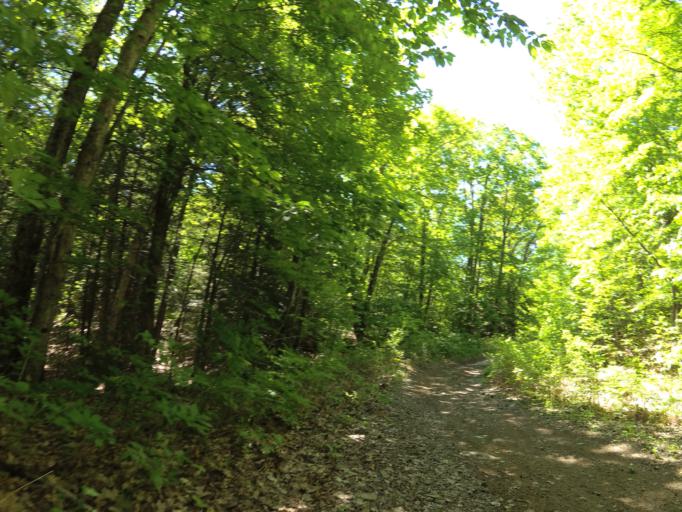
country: CA
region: Ontario
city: Renfrew
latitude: 45.0516
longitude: -77.0881
